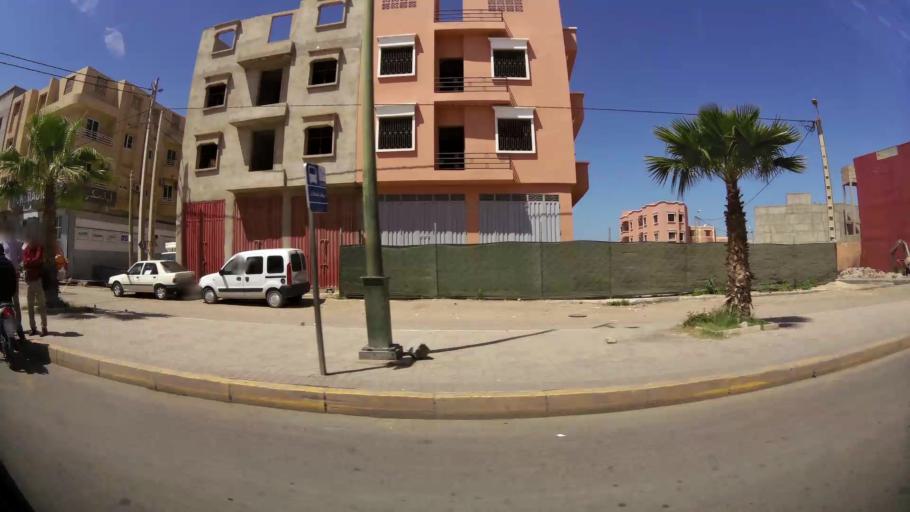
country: MA
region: Souss-Massa-Draa
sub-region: Inezgane-Ait Mellou
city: Inezgane
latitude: 30.3138
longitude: -9.5029
